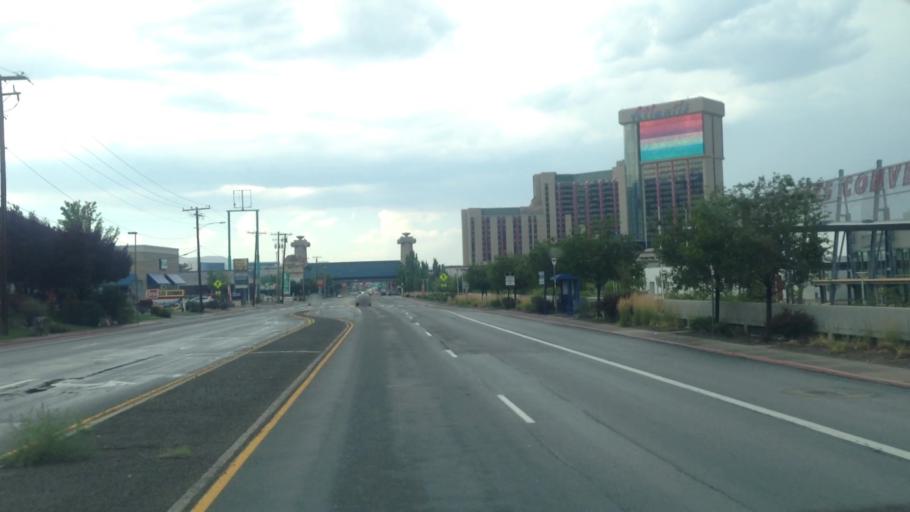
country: US
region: Nevada
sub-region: Washoe County
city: Reno
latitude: 39.4845
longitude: -119.7928
